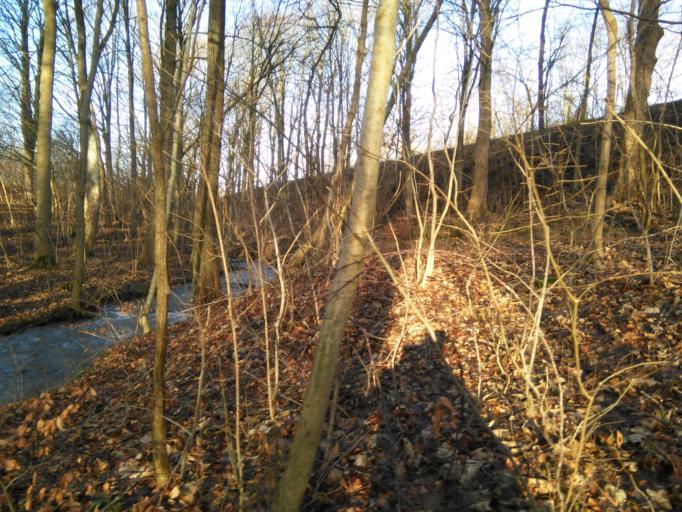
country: DK
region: Central Jutland
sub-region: Arhus Kommune
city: Stavtrup
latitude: 56.1575
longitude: 10.0850
